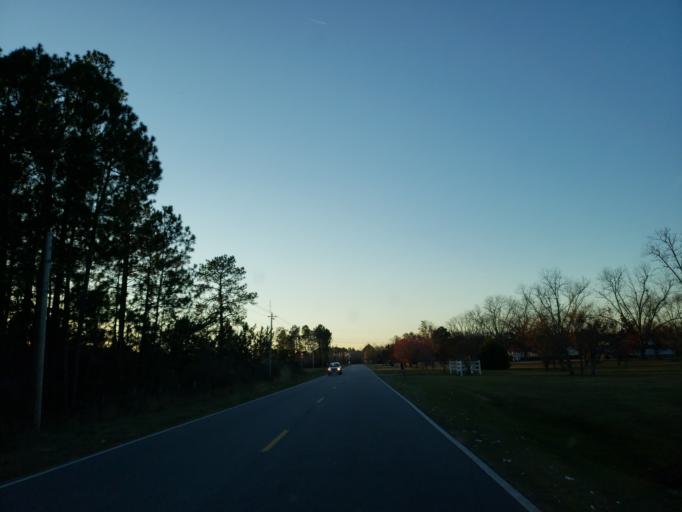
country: US
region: Georgia
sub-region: Crisp County
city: Cordele
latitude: 31.9267
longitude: -83.7666
